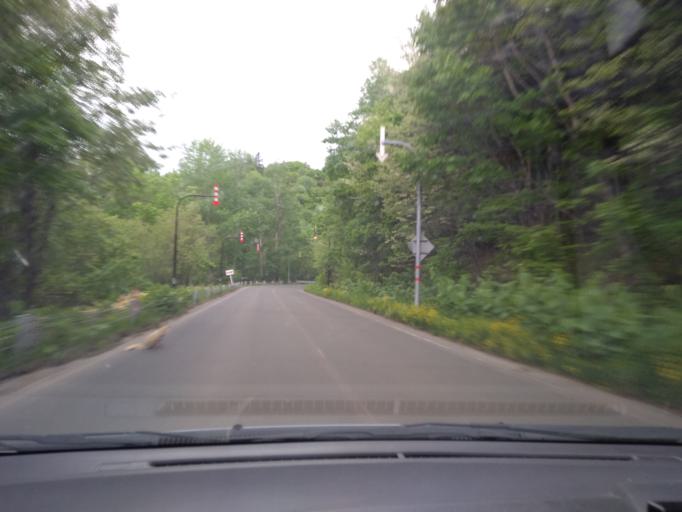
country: JP
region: Hokkaido
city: Shimo-furano
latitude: 43.1385
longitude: 142.4682
